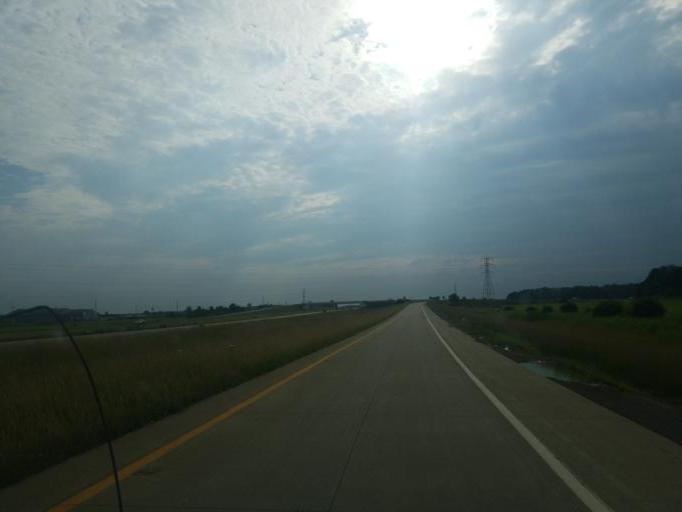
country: US
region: Ohio
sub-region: Wayne County
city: Smithville
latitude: 40.8084
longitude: -81.8500
